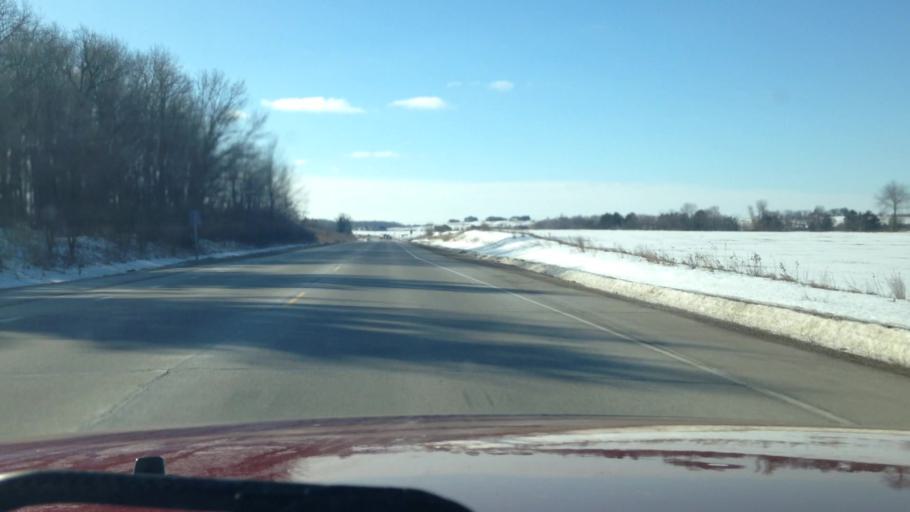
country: US
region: Wisconsin
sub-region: Waukesha County
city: Oconomowoc
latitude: 43.1850
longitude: -88.5086
